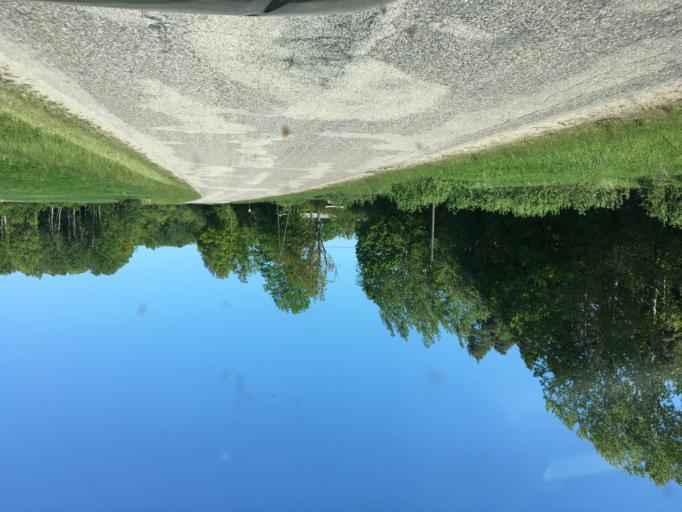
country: LV
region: Dundaga
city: Dundaga
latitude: 57.4932
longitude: 22.3440
